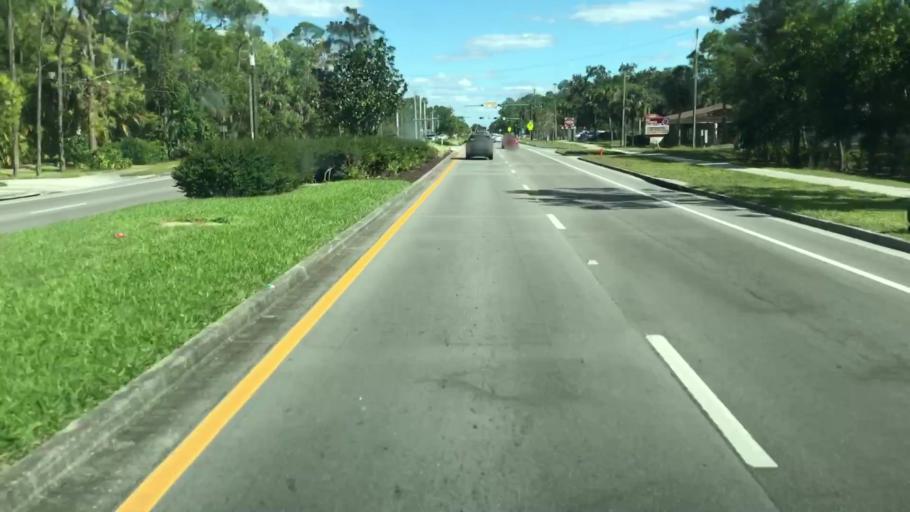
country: US
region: Florida
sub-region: Collier County
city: Vineyards
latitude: 26.2290
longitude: -81.6738
